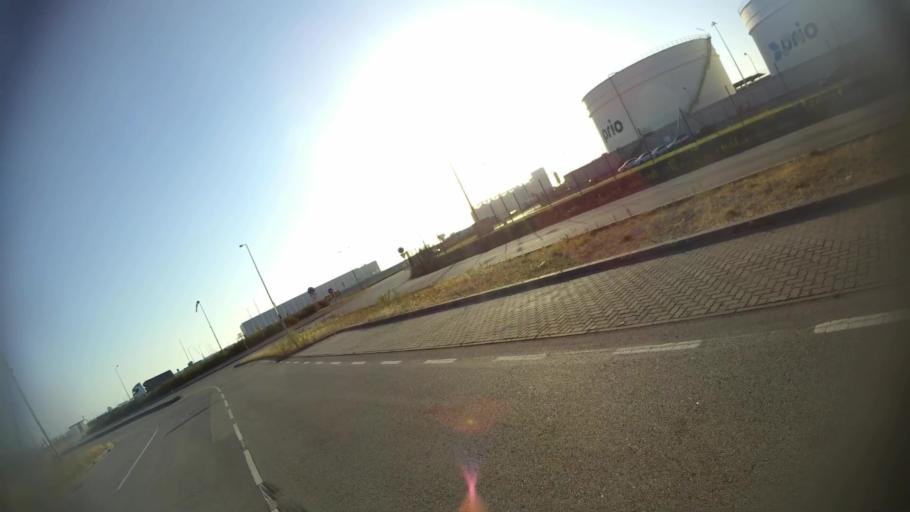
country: PT
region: Aveiro
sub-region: Ilhavo
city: Gafanha da Nazare
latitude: 40.6513
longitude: -8.7044
